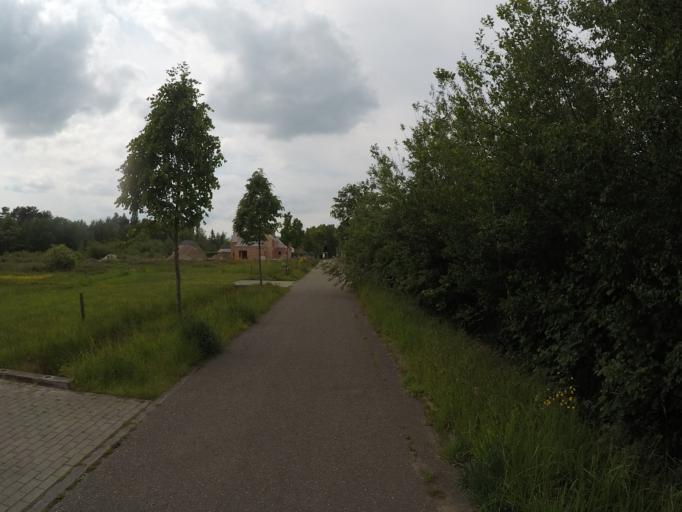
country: BE
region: Flanders
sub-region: Provincie Antwerpen
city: Zoersel
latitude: 51.2764
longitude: 4.6600
